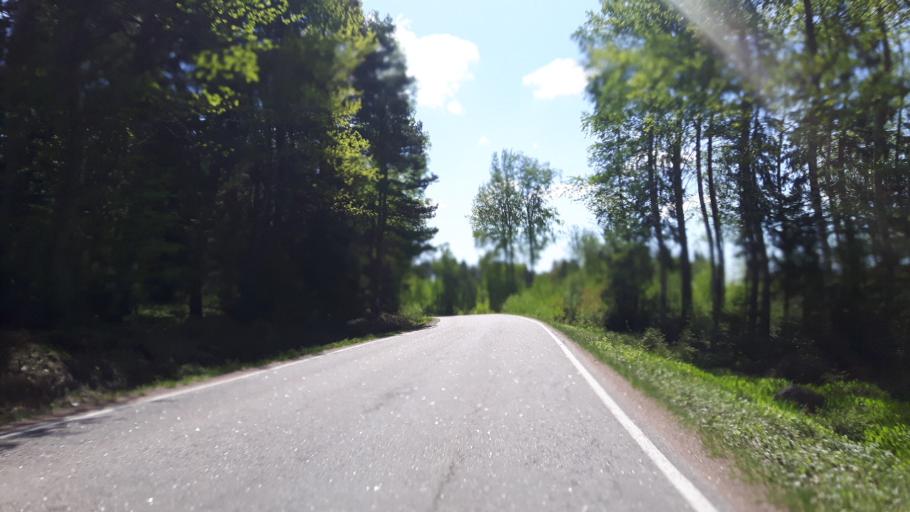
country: FI
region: Kymenlaakso
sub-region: Kotka-Hamina
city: Hamina
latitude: 60.5298
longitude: 27.2932
